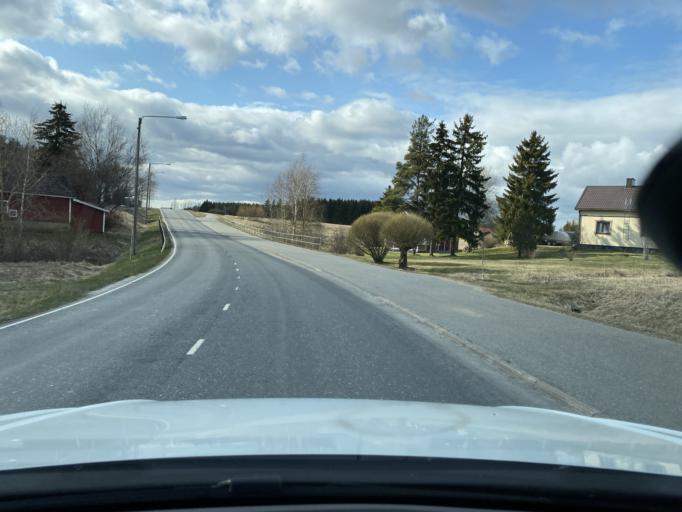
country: FI
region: Pirkanmaa
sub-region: Lounais-Pirkanmaa
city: Punkalaidun
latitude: 61.1194
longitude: 23.0845
